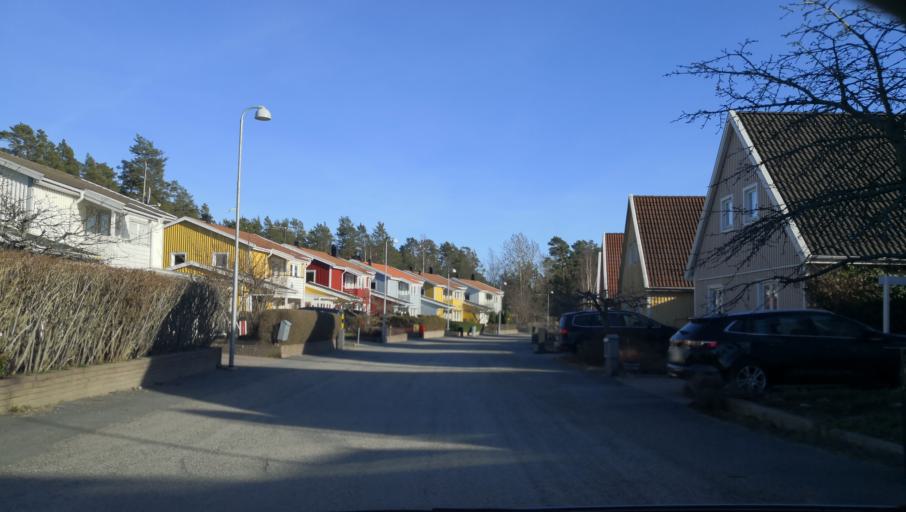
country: SE
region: Stockholm
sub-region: Varmdo Kommun
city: Gustavsberg
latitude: 59.3380
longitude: 18.3783
